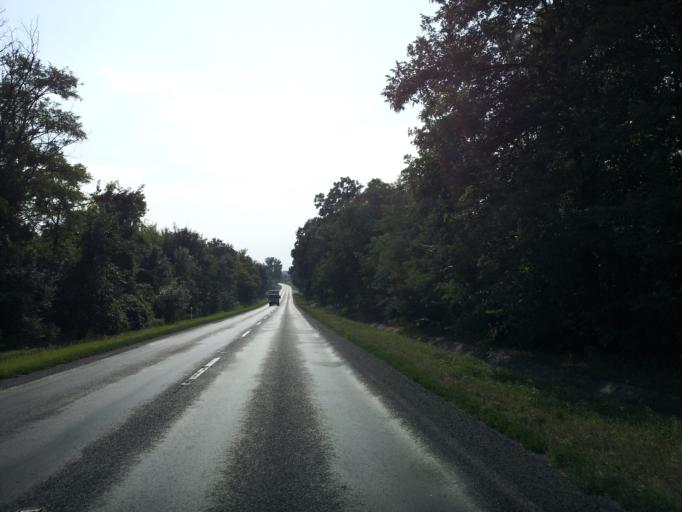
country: HU
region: Somogy
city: Balatonszabadi
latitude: 46.9411
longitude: 18.1607
